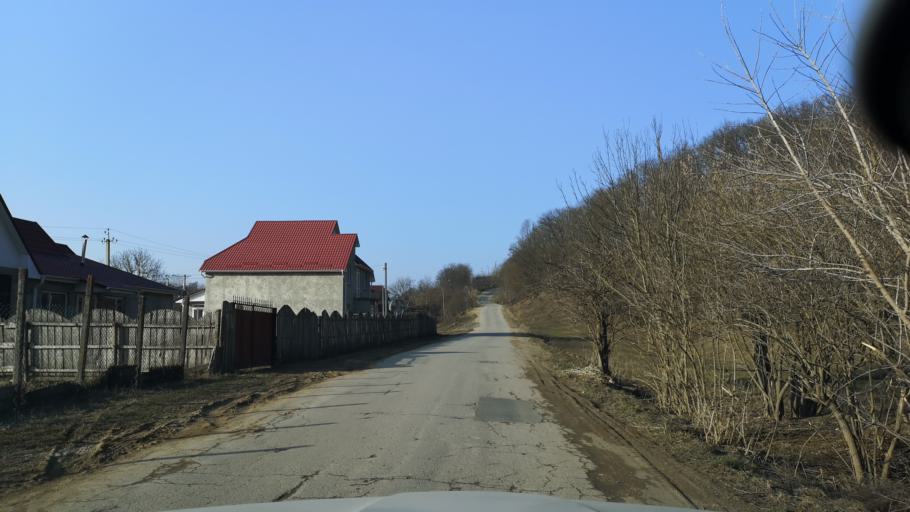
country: MD
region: Nisporeni
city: Nisporeni
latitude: 47.0880
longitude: 28.3180
